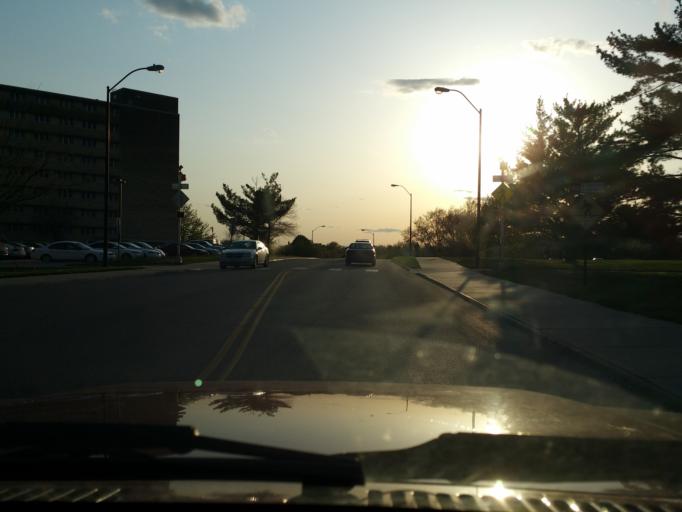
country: US
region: Kansas
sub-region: Riley County
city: Manhattan
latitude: 39.1952
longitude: -96.5767
